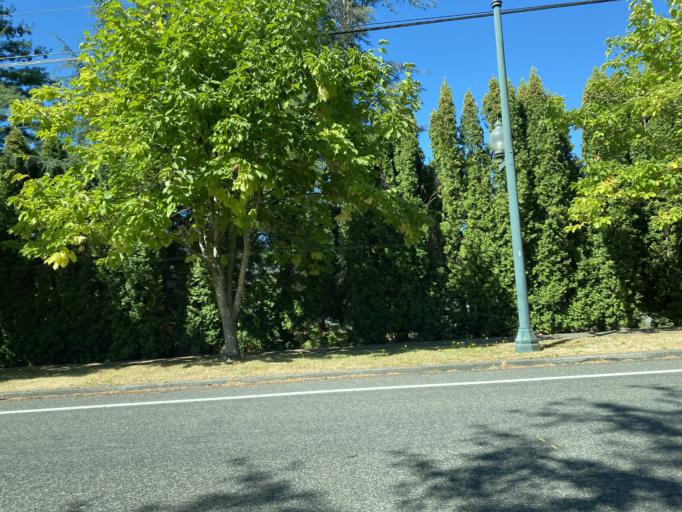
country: US
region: Washington
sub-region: Thurston County
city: Tumwater
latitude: 47.0086
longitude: -122.8652
